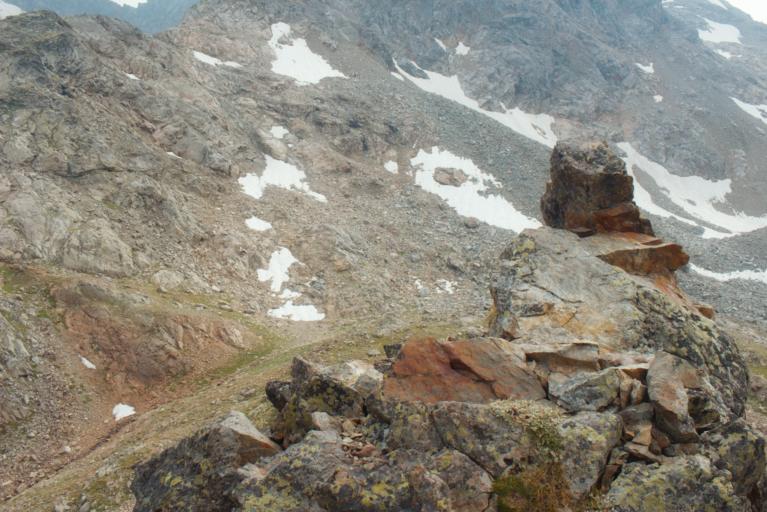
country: RU
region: Karachayevo-Cherkesiya
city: Nizhniy Arkhyz
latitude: 43.4582
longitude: 41.2280
